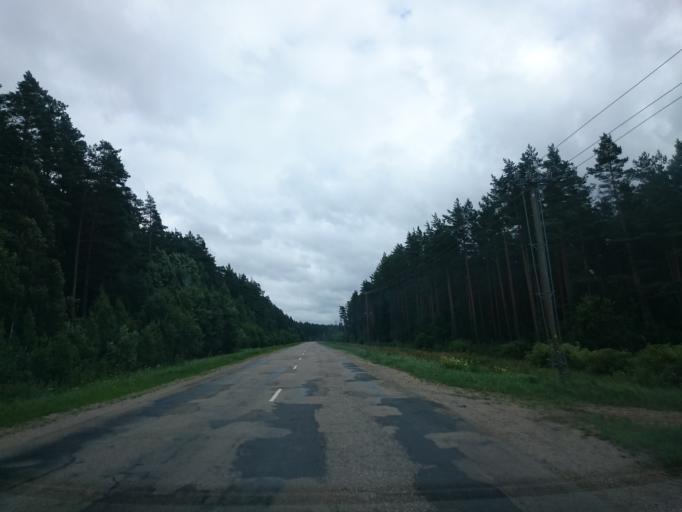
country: LV
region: Pavilostas
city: Pavilosta
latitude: 56.7949
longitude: 21.2368
